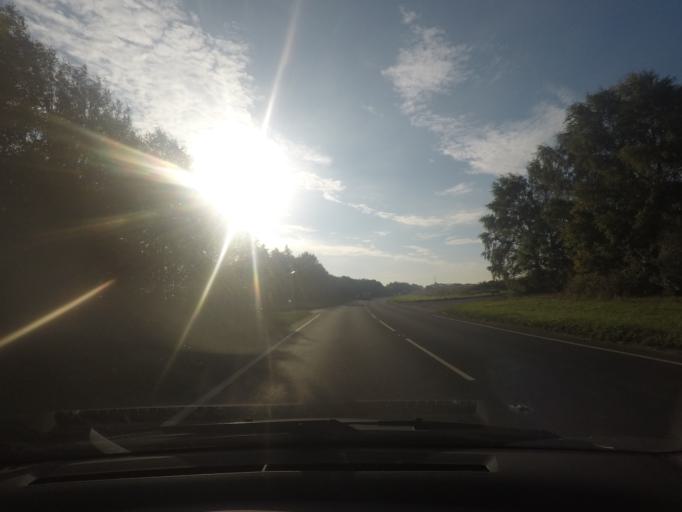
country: GB
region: England
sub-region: East Riding of Yorkshire
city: Londesborough
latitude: 53.8687
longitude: -0.6850
